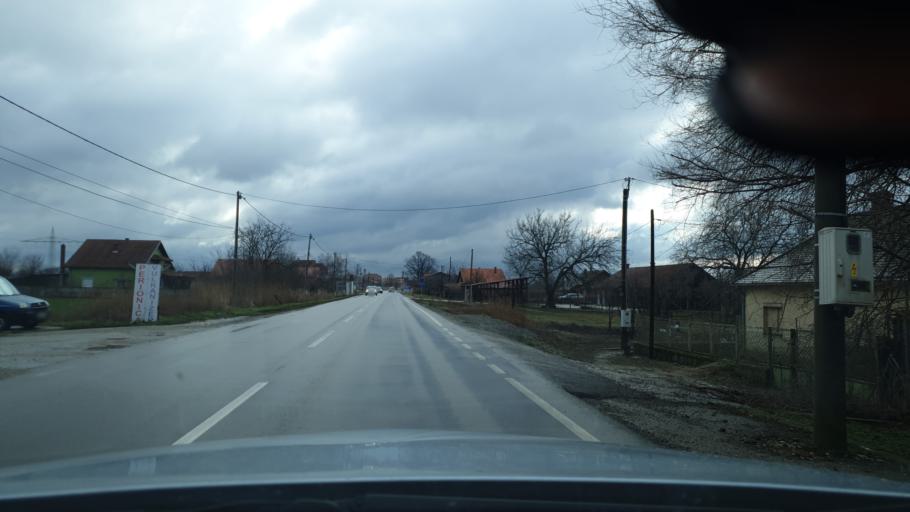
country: RS
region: Central Serbia
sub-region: Branicevski Okrug
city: Malo Crnice
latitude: 44.5664
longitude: 21.2943
